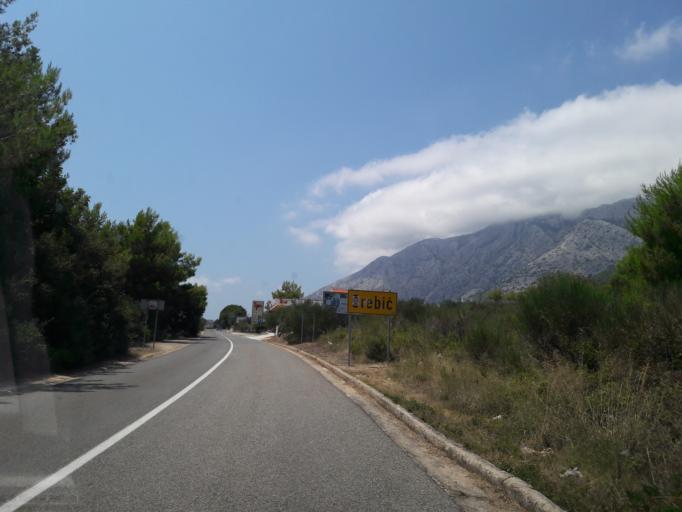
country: HR
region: Dubrovacko-Neretvanska
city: Orebic
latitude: 42.9839
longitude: 17.2017
